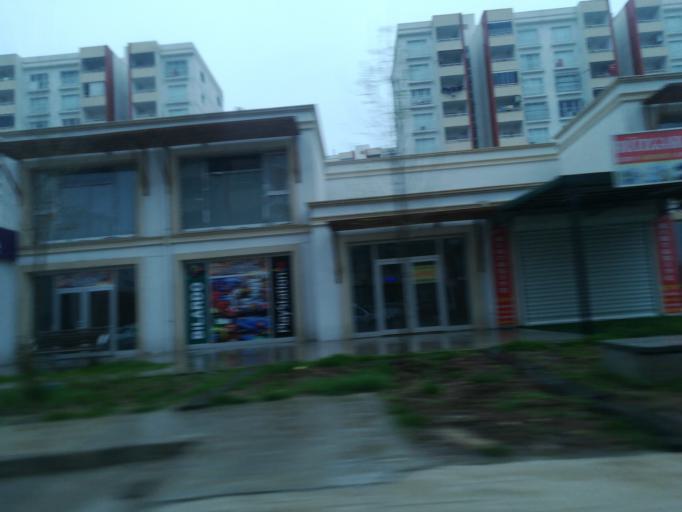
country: TR
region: Adana
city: Seyhan
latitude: 37.0089
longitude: 35.2771
